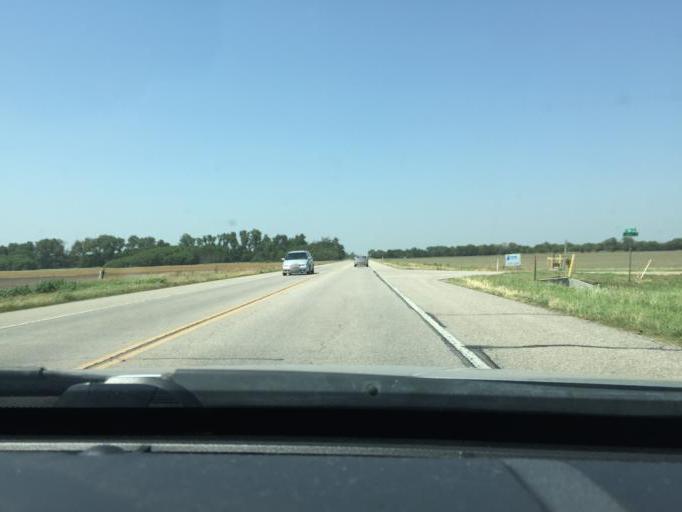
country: US
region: Kansas
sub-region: Reno County
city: South Hutchinson
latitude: 37.9988
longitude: -97.8668
